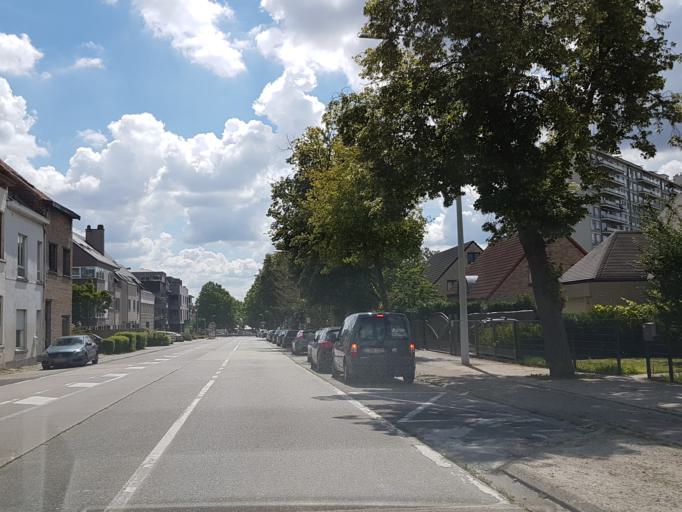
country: BE
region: Flanders
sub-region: Provincie Vlaams-Brabant
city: Dilbeek
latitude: 50.8862
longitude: 4.2710
